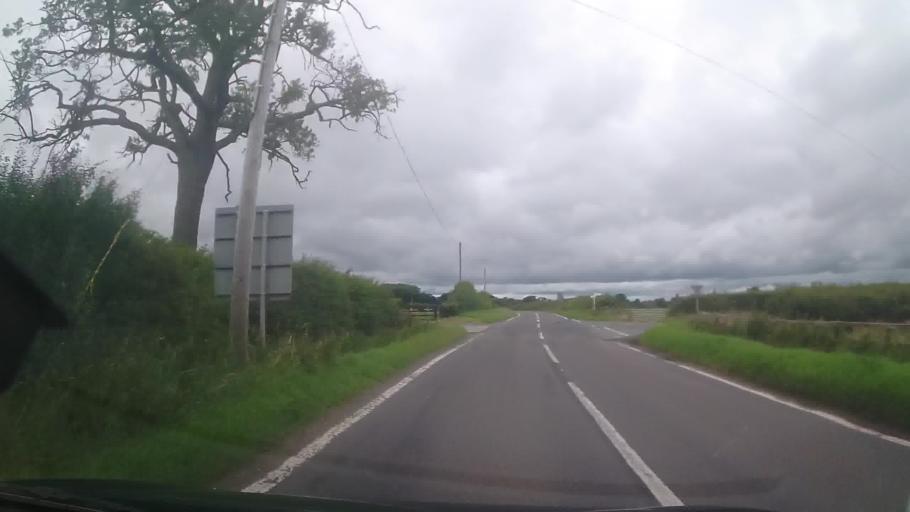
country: GB
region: England
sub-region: Shropshire
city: Petton
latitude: 52.8201
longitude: -2.7952
